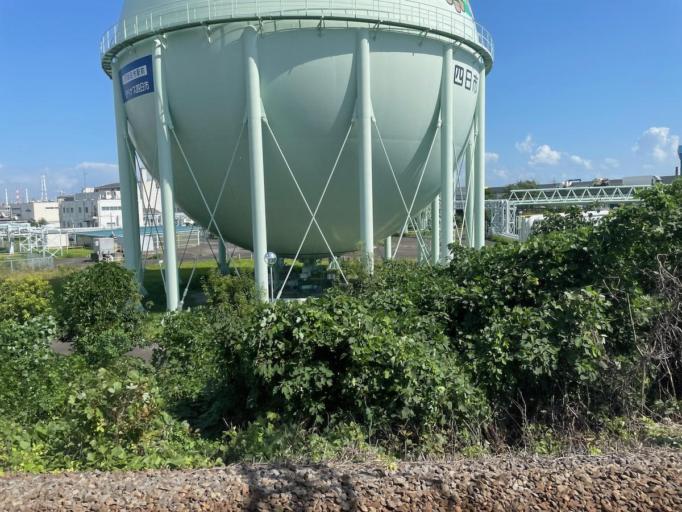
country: JP
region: Mie
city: Yokkaichi
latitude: 34.9500
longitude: 136.6212
